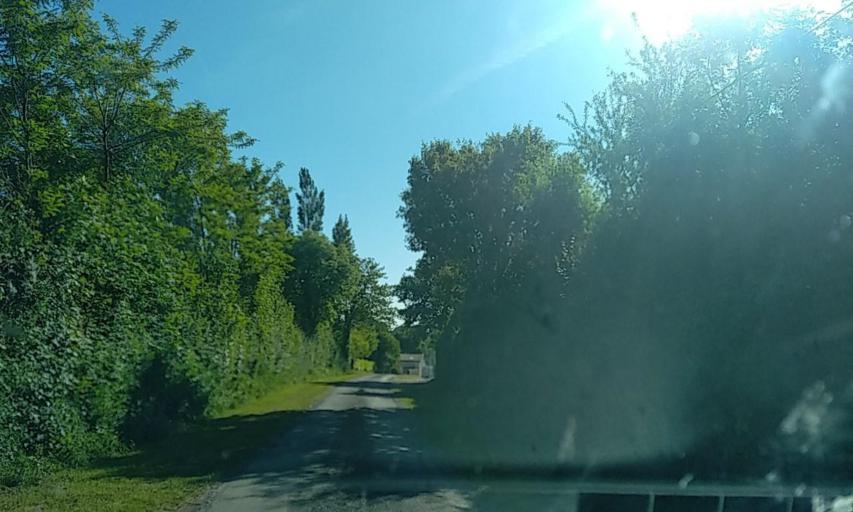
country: FR
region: Poitou-Charentes
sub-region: Departement des Deux-Sevres
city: Boisme
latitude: 46.7961
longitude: -0.4390
